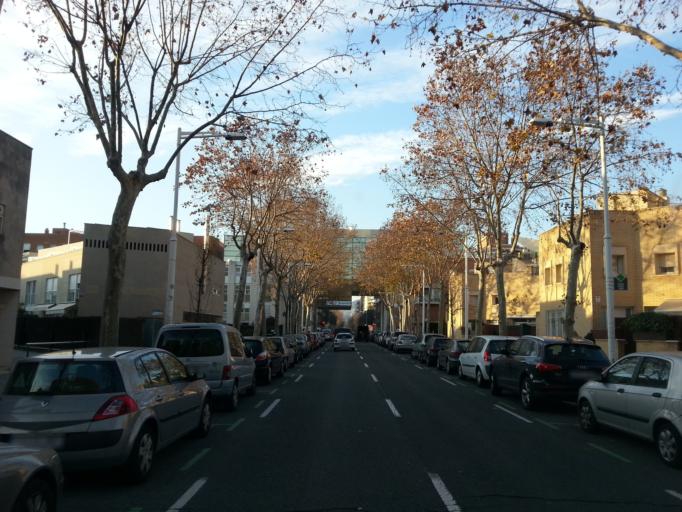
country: ES
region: Catalonia
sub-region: Provincia de Barcelona
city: Ciutat Vella
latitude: 41.3913
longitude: 2.1961
